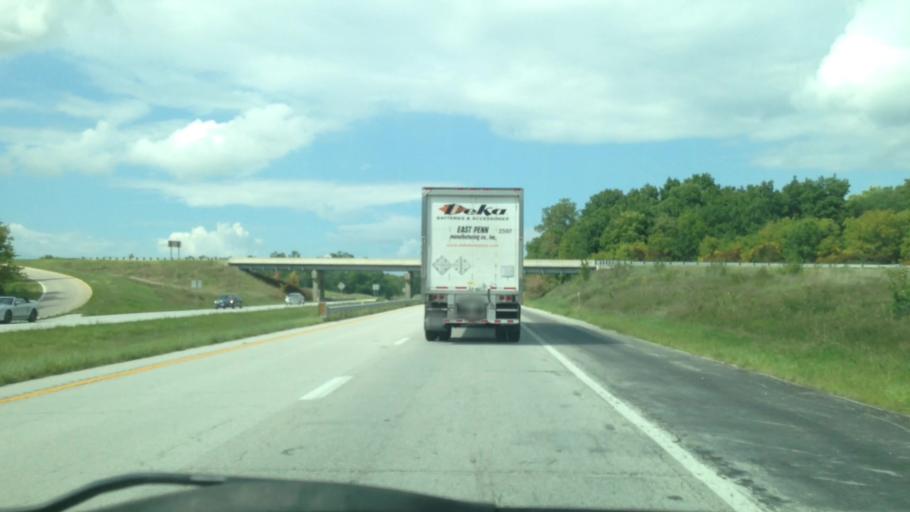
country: US
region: Missouri
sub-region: Marion County
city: Palmyra
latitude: 39.7669
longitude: -91.5189
